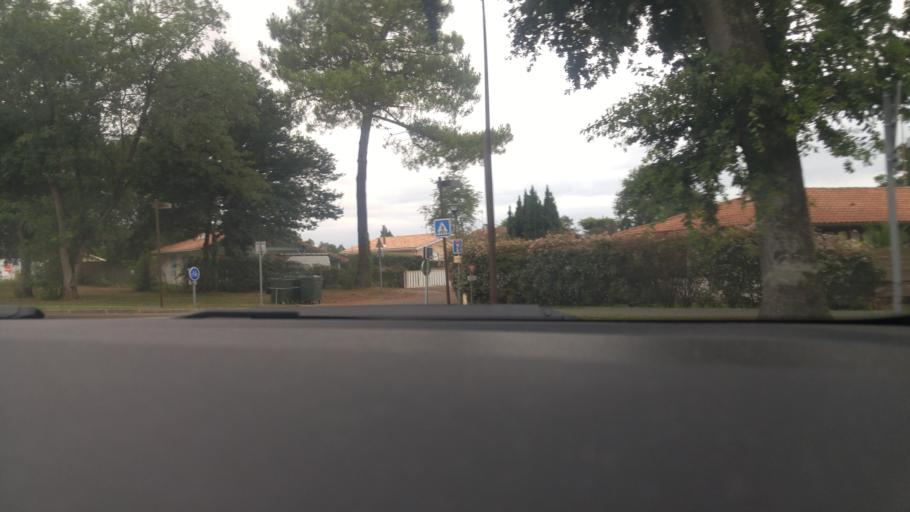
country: FR
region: Aquitaine
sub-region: Departement des Landes
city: Soustons
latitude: 43.7483
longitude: -1.3195
